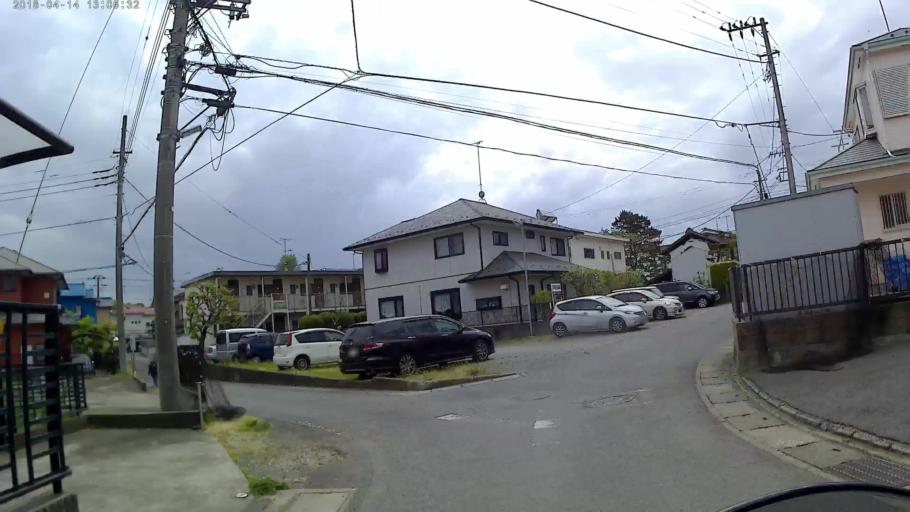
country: JP
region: Kanagawa
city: Isehara
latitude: 35.3601
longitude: 139.2893
